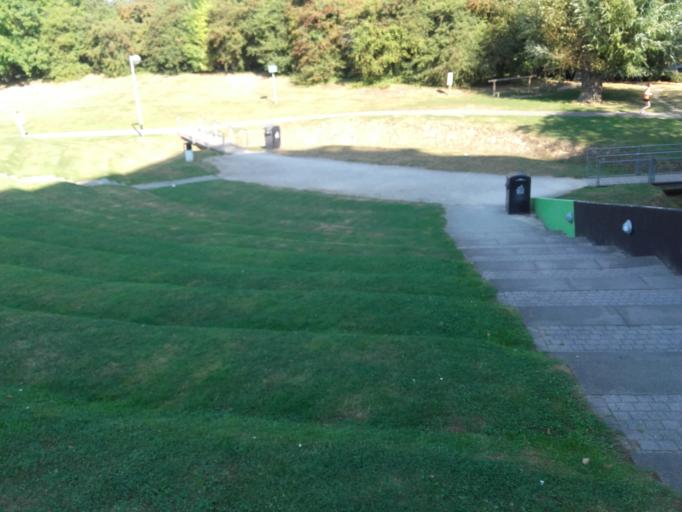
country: BE
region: Brussels Capital
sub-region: Bruxelles-Capitale
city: Brussels
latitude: 50.8217
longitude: 4.3950
